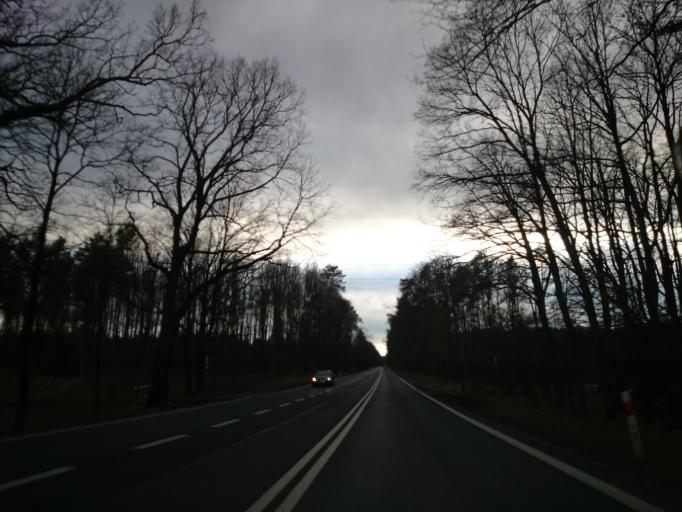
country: PL
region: Opole Voivodeship
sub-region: Powiat opolski
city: Dabrowa
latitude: 50.6815
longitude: 17.7201
